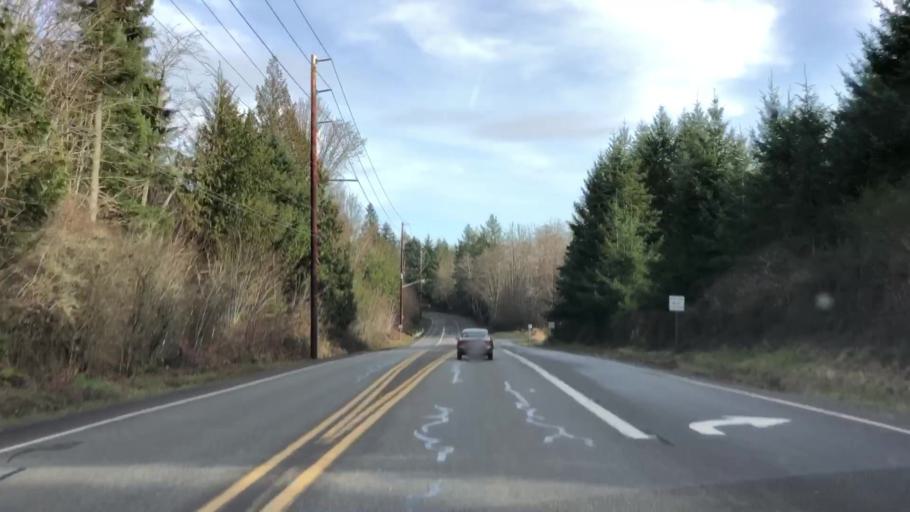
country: US
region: Washington
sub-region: Kitsap County
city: Indianola
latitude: 47.7846
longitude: -122.5472
